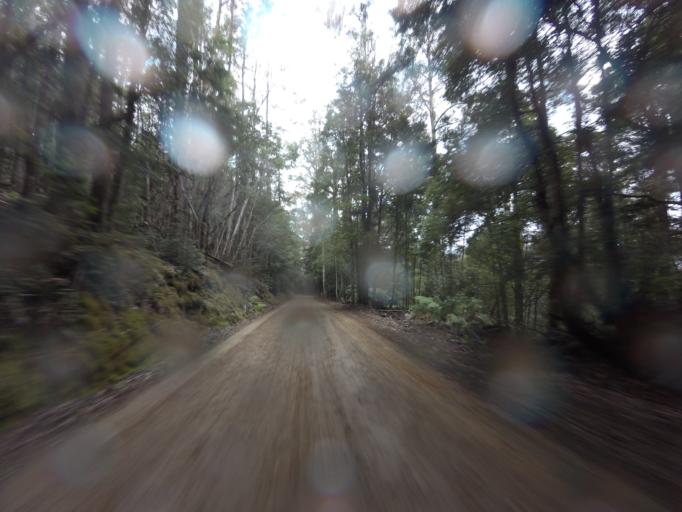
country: AU
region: Tasmania
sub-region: Derwent Valley
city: New Norfolk
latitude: -42.6805
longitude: 146.6826
